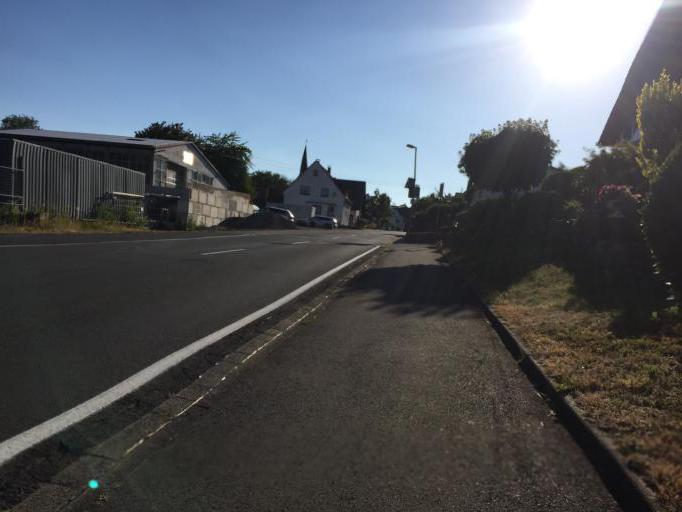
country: DE
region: Rheinland-Pfalz
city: Hartlingen
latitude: 50.5245
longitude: 7.8940
